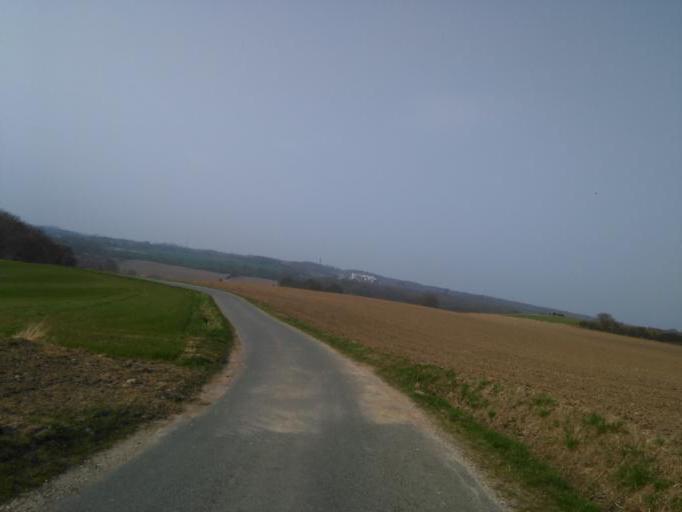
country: DK
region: Central Jutland
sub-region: Arhus Kommune
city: Beder
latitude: 56.0708
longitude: 10.2273
